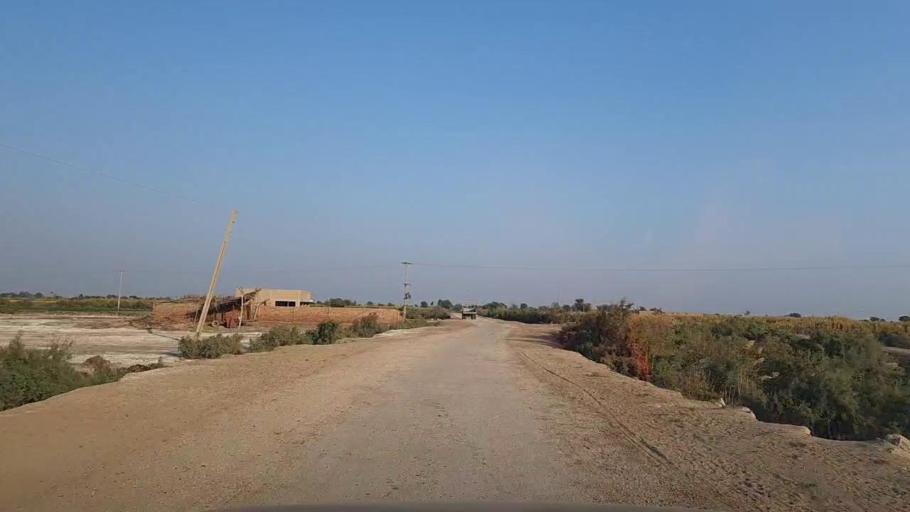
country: PK
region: Sindh
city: Tando Mittha Khan
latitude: 25.9354
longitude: 69.0970
